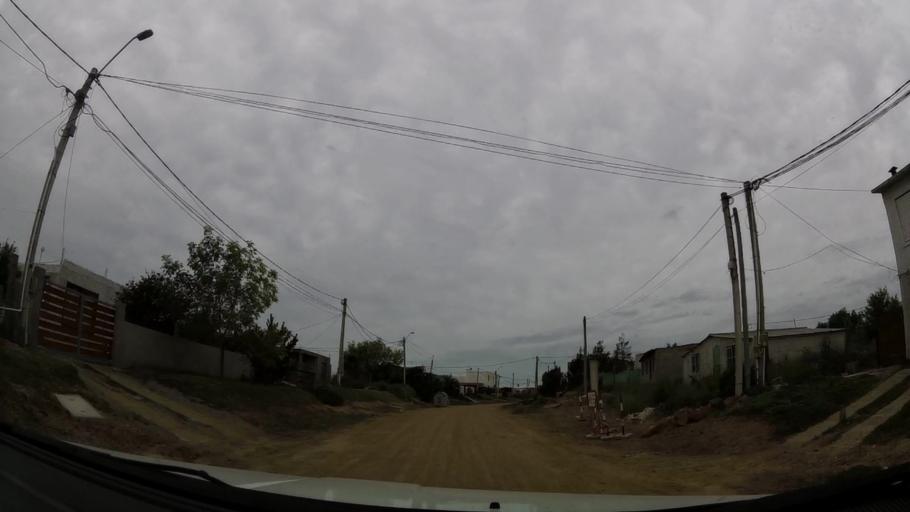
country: UY
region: Maldonado
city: Maldonado
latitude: -34.8826
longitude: -54.9399
